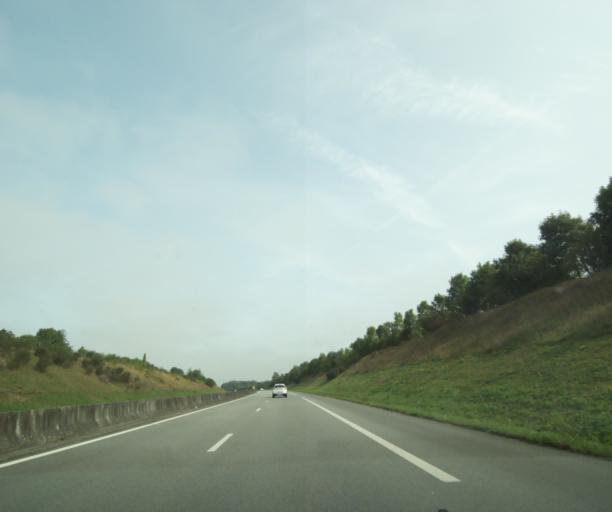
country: FR
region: Lower Normandy
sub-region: Departement de l'Orne
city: Sees
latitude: 48.5530
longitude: 0.1768
